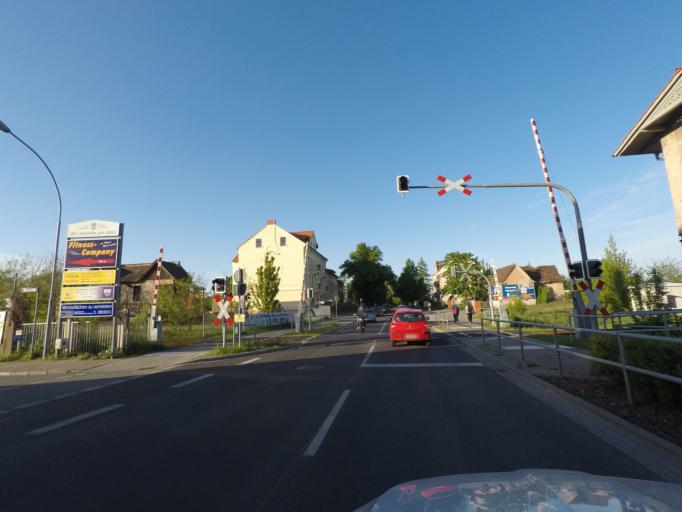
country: DE
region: Brandenburg
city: Bad Freienwalde
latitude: 52.7904
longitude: 14.0345
